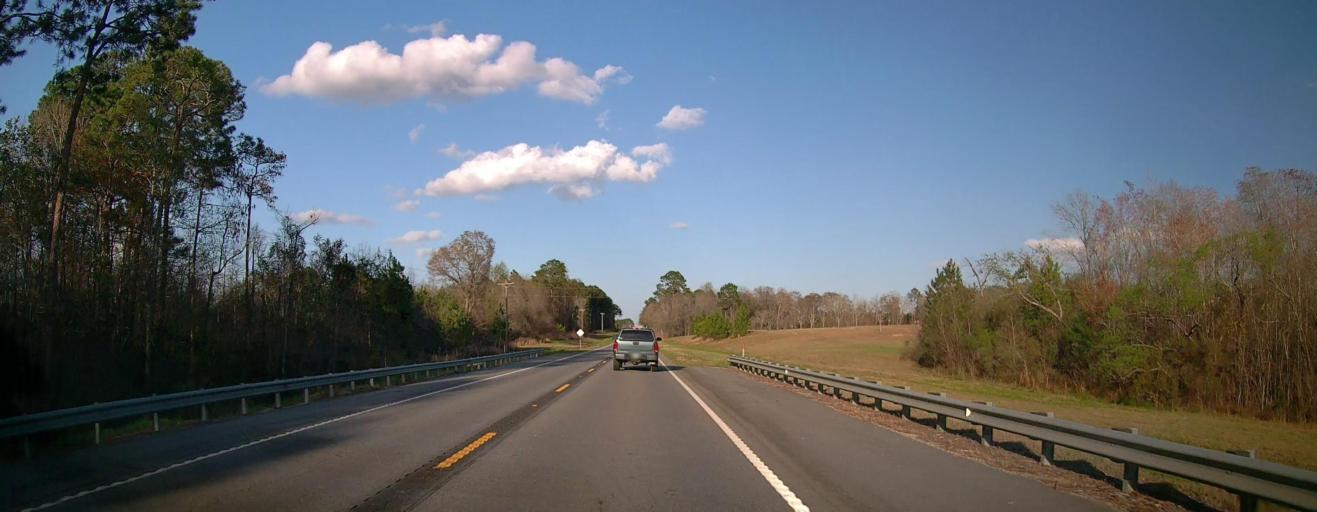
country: US
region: Georgia
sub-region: Tattnall County
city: Reidsville
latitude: 32.1309
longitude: -82.0500
